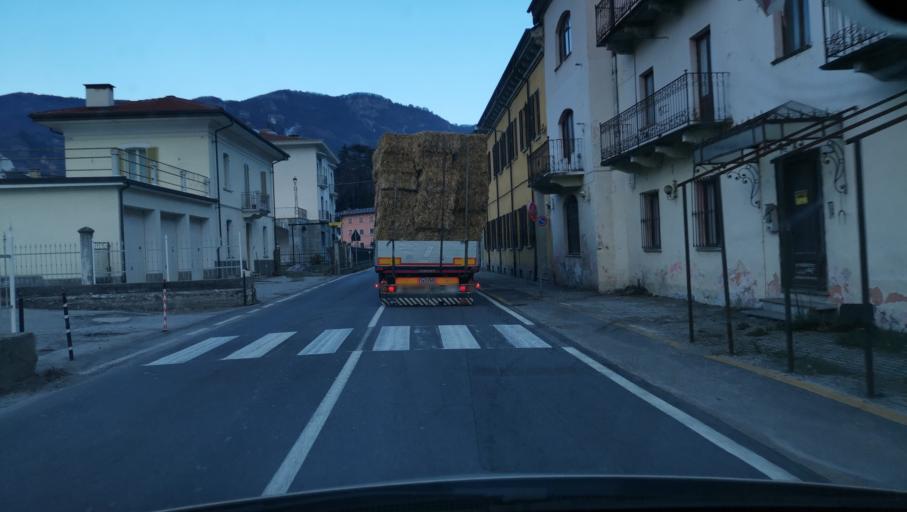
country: IT
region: Piedmont
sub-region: Provincia di Cuneo
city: Demonte
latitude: 44.3139
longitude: 7.2921
